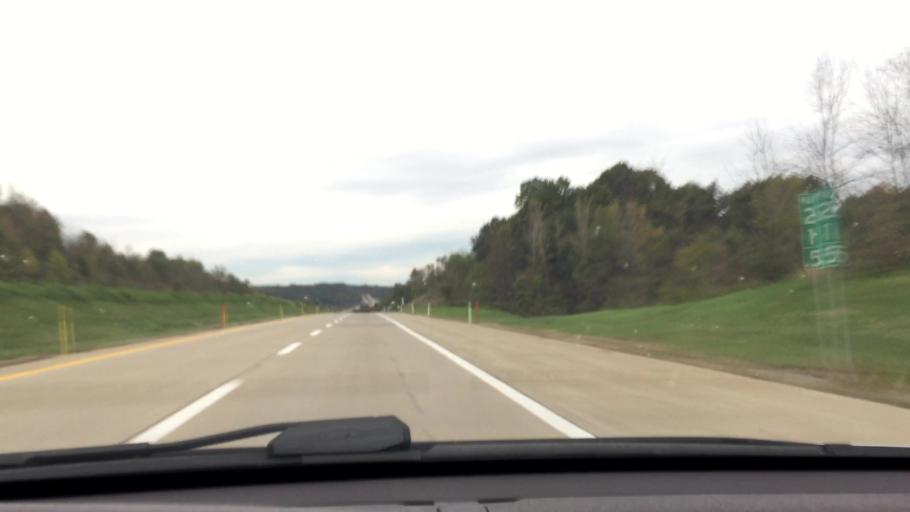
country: US
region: Pennsylvania
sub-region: Lawrence County
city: New Beaver
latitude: 40.8977
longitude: -80.3753
